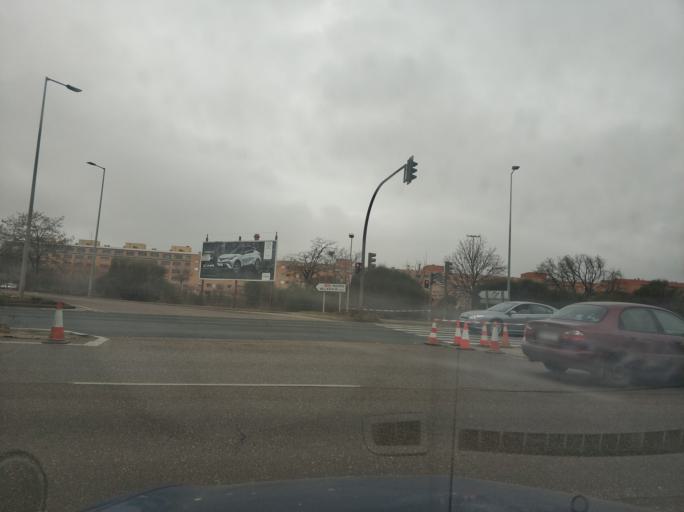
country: ES
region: Castille and Leon
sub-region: Provincia de Valladolid
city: Valladolid
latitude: 41.6416
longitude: -4.7021
